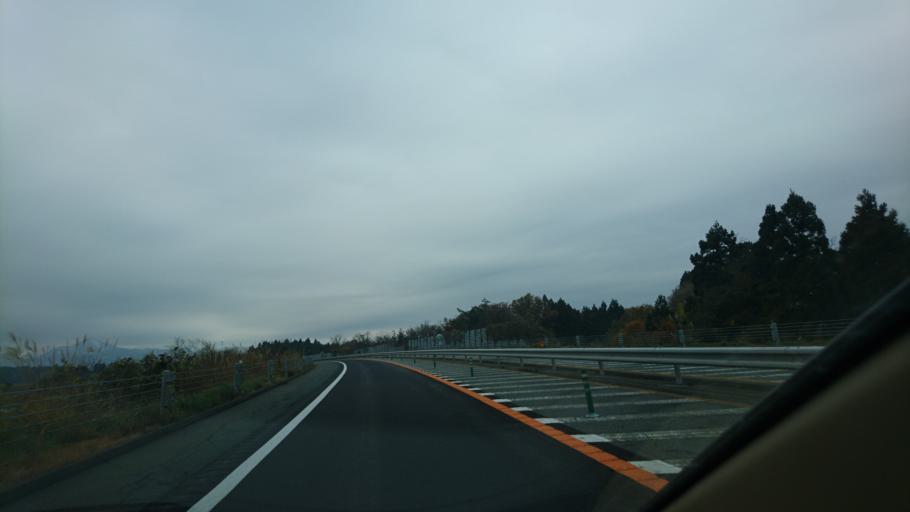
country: JP
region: Iwate
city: Kitakami
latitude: 39.2793
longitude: 141.0628
